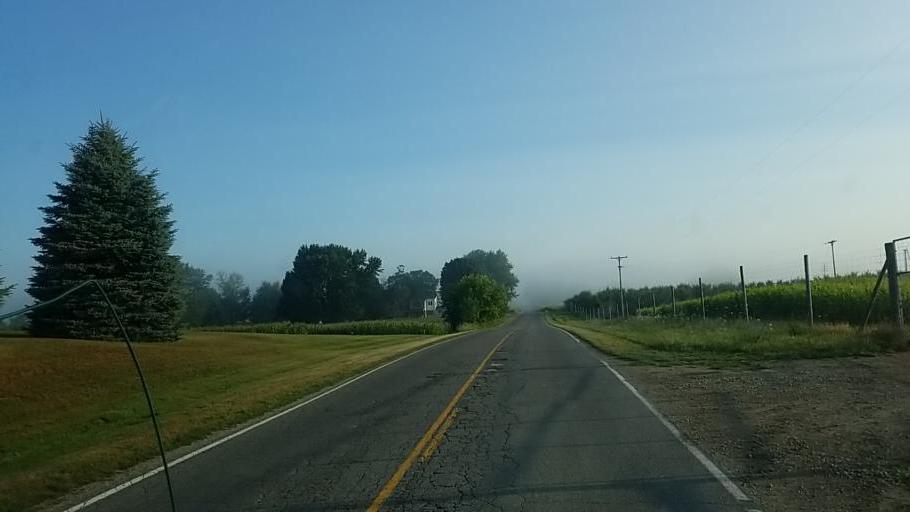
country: US
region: Michigan
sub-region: Newaygo County
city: Fremont
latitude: 43.4613
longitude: -86.0191
